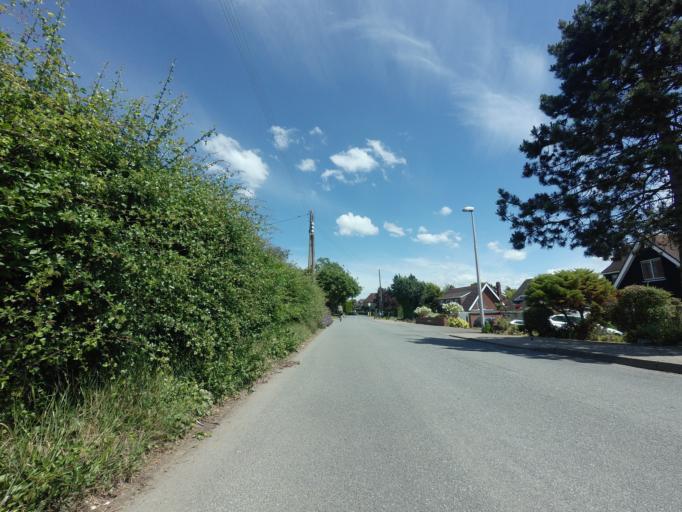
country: GB
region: England
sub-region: Medway
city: High Halstow
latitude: 51.4482
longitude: 0.5590
